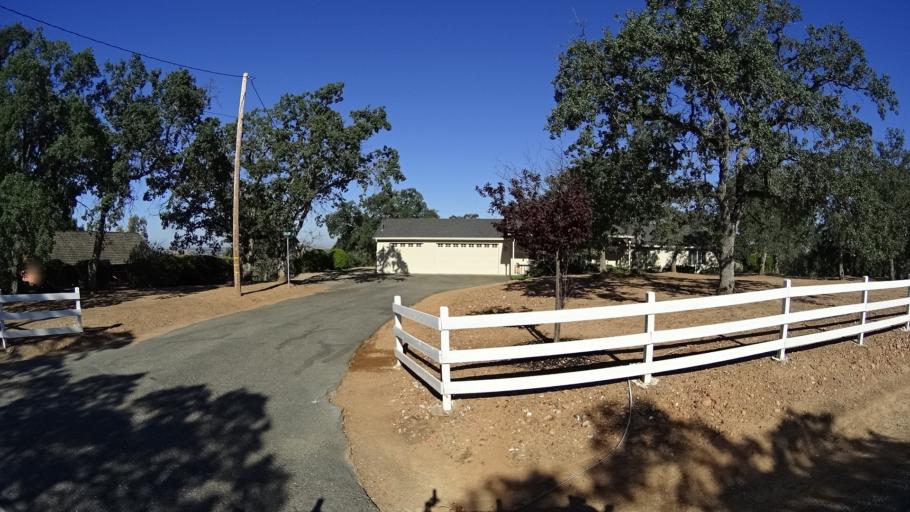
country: US
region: California
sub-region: Calaveras County
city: Rancho Calaveras
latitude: 38.1166
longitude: -120.8690
